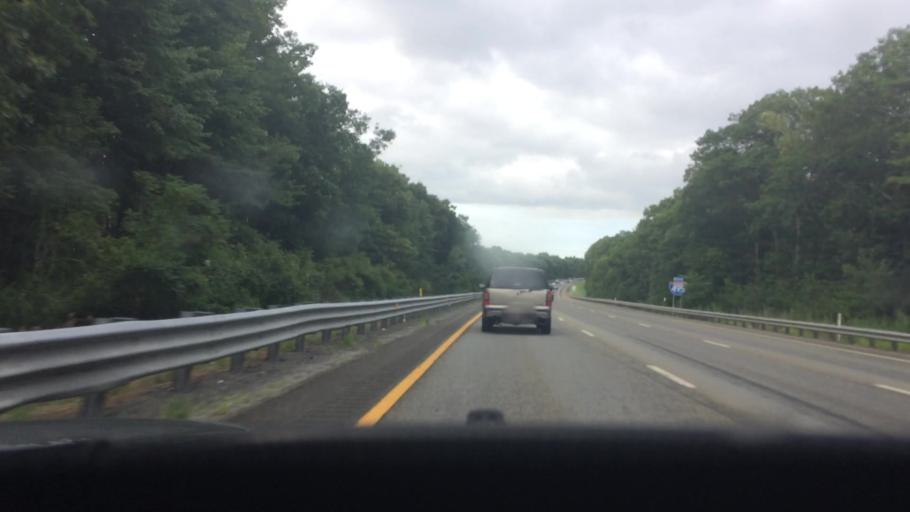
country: US
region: Massachusetts
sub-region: Worcester County
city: Harvard
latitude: 42.4918
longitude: -71.5409
